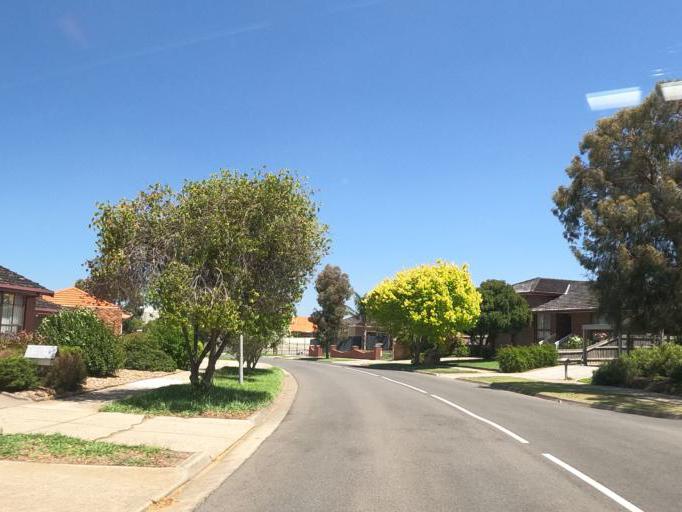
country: AU
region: Victoria
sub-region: Hume
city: Greenvale
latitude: -37.6373
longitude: 144.8833
